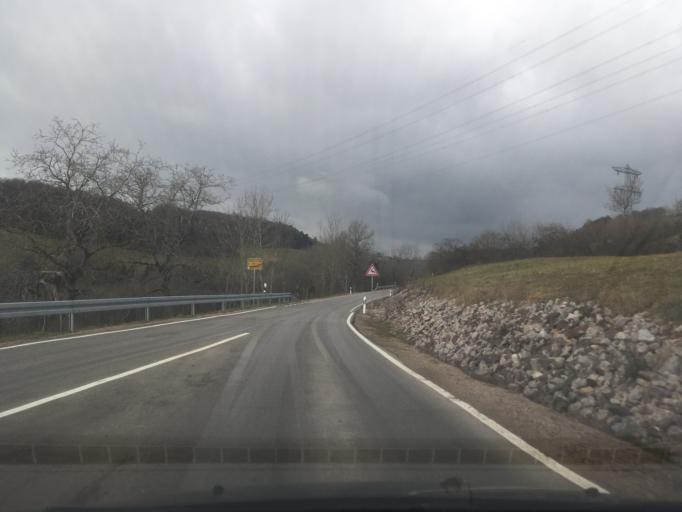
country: DE
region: Baden-Wuerttemberg
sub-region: Freiburg Region
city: Waldshut-Tiengen
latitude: 47.6550
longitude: 8.1929
